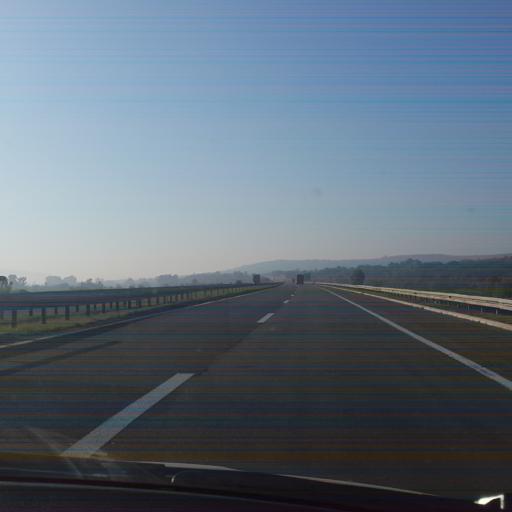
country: RS
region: Central Serbia
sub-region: Nisavski Okrug
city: Merosina
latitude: 43.2967
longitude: 21.7988
